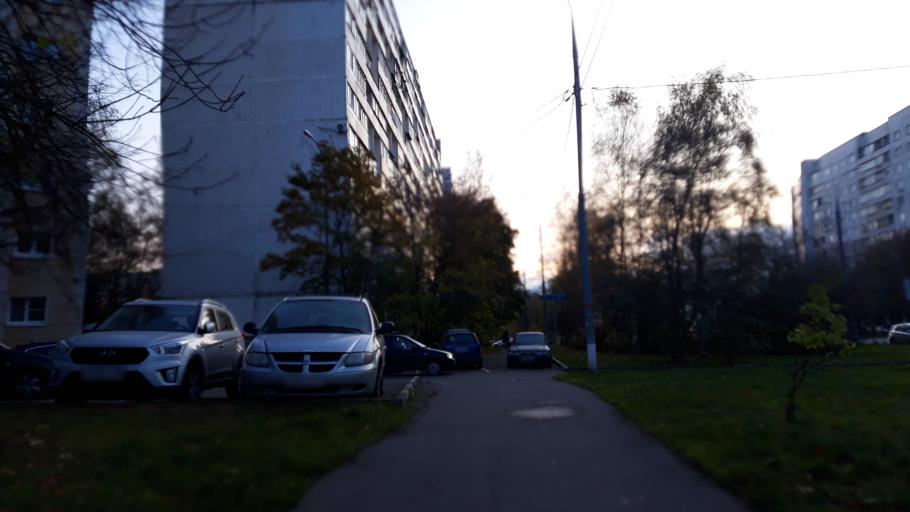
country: RU
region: Moscow
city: Zelenograd
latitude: 55.9854
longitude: 37.1815
